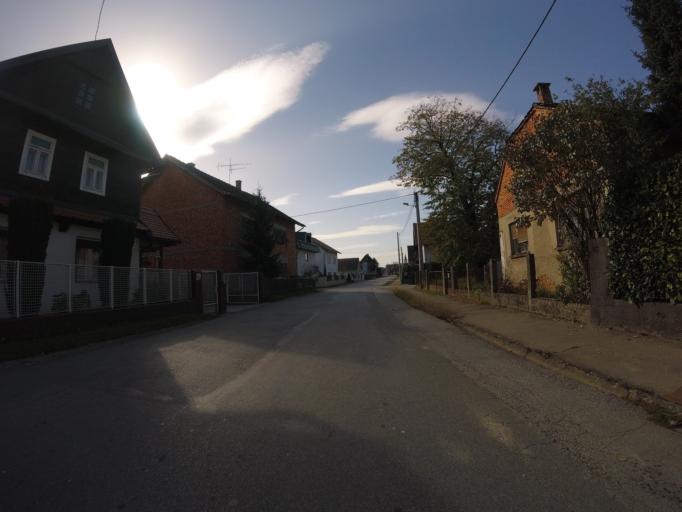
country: HR
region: Zagrebacka
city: Mraclin
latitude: 45.6684
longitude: 16.1011
